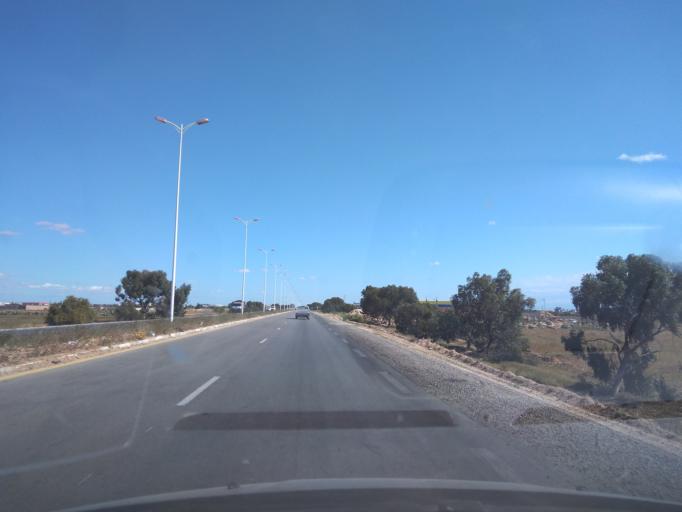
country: TN
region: Safaqis
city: Al Qarmadah
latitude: 34.8482
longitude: 10.7491
